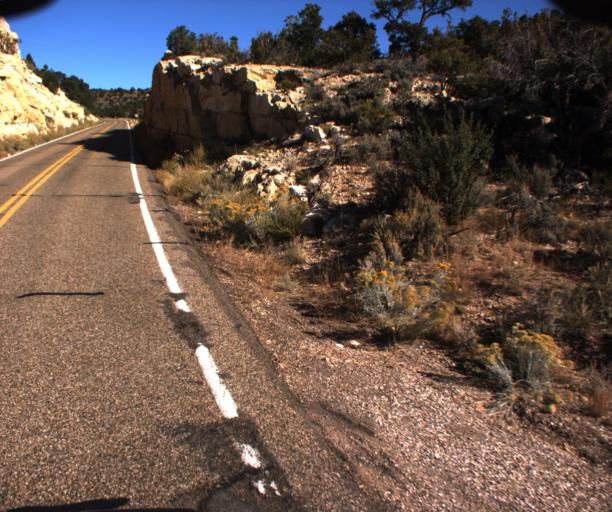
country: US
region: Arizona
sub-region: Coconino County
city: Fredonia
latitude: 36.7265
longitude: -112.0864
